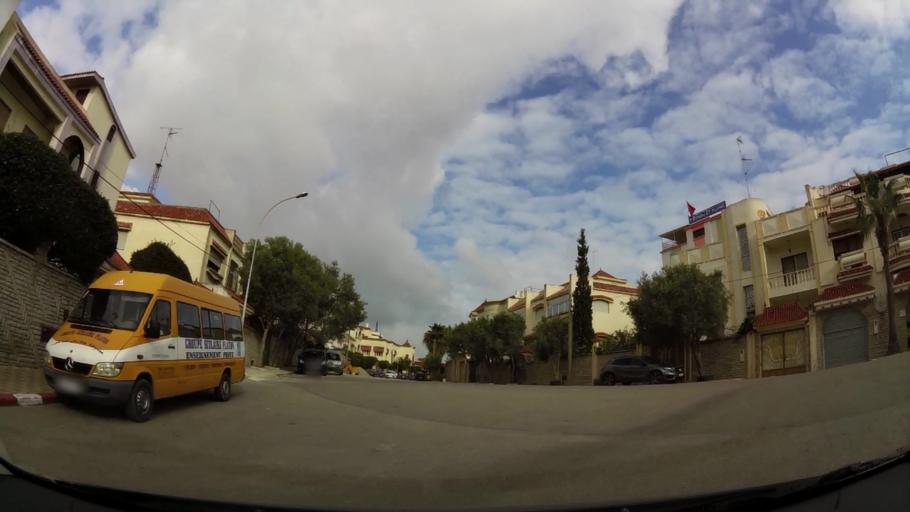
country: MA
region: Tanger-Tetouan
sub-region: Tanger-Assilah
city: Tangier
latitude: 35.7604
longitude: -5.8288
